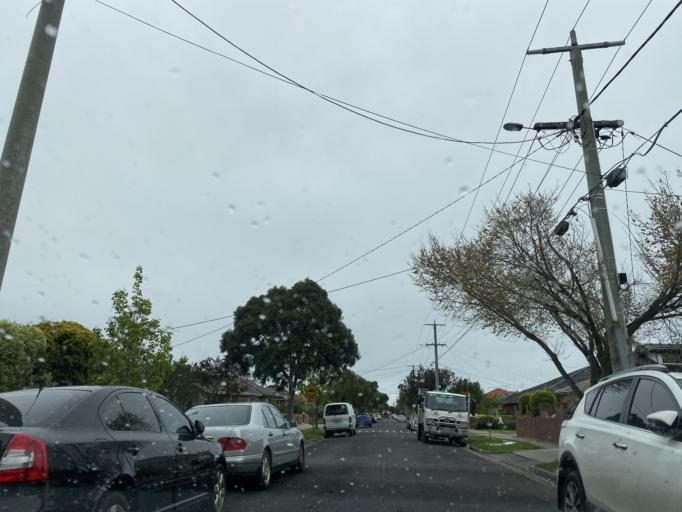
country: AU
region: Victoria
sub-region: Moreland
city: Fawkner
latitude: -37.7078
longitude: 144.9668
